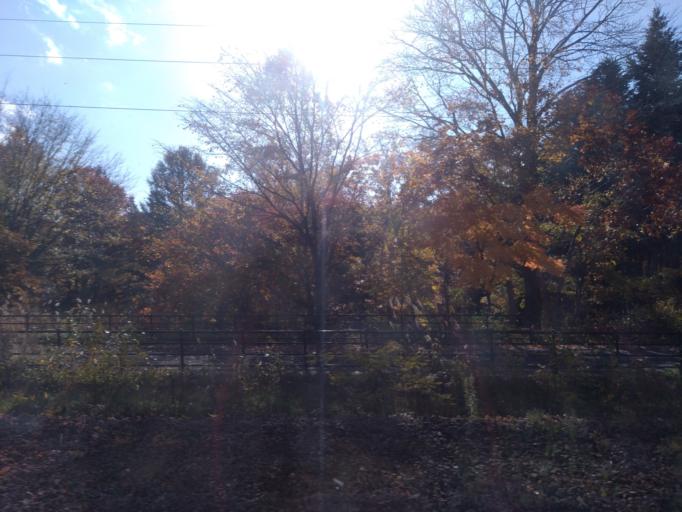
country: JP
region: Hokkaido
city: Kitahiroshima
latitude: 42.9969
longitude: 141.5347
